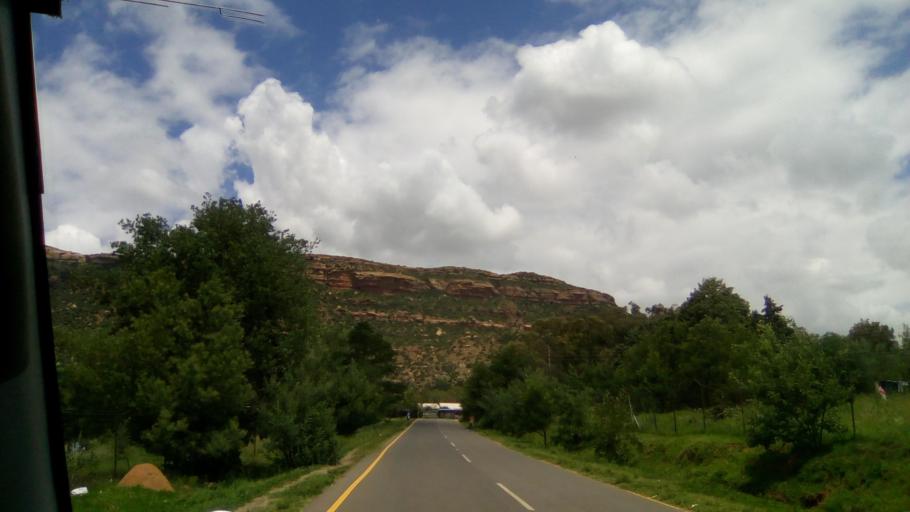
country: LS
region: Maseru
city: Nako
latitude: -29.6288
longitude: 27.5023
